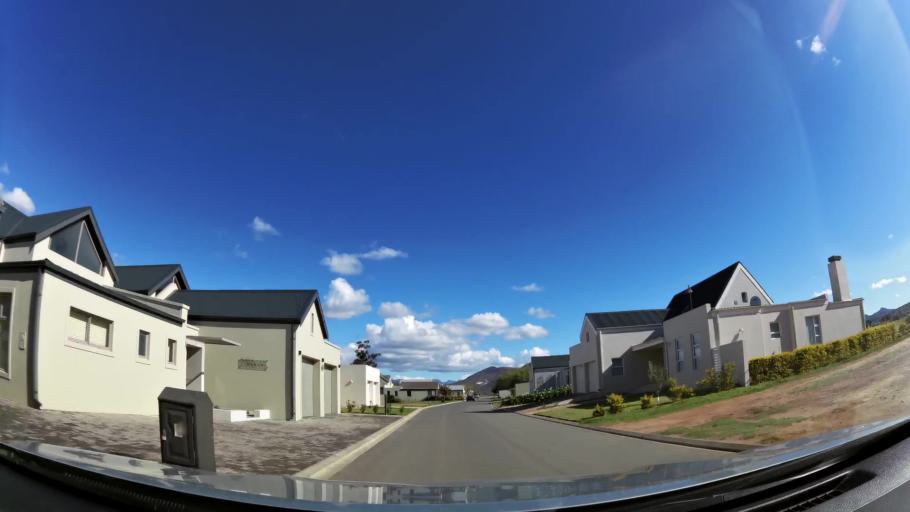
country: ZA
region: Western Cape
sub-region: Cape Winelands District Municipality
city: Ashton
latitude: -33.8121
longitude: 19.8491
